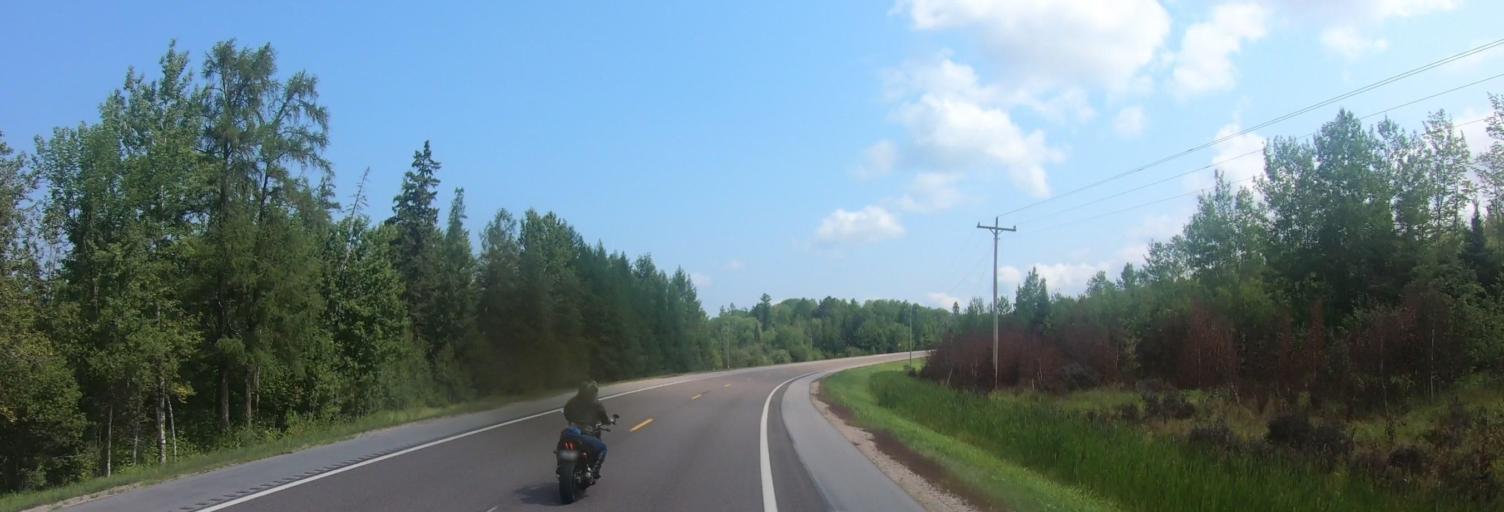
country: US
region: Minnesota
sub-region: Saint Louis County
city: Mountain Iron
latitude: 48.0548
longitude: -92.7978
